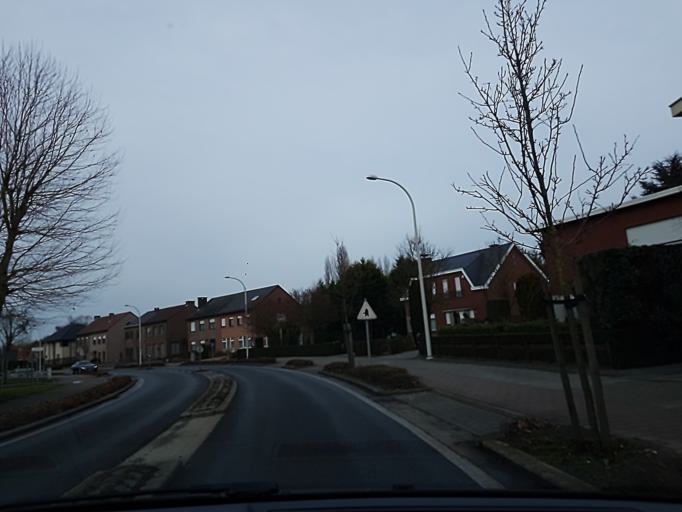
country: BE
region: Flanders
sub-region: Provincie Antwerpen
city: Lier
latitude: 51.1001
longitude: 4.6072
